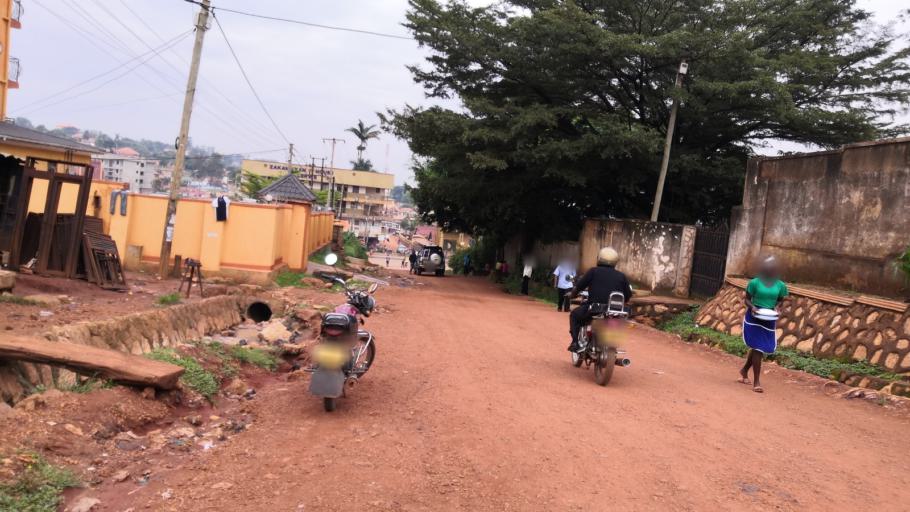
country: UG
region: Central Region
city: Kampala Central Division
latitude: 0.3465
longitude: 32.5722
